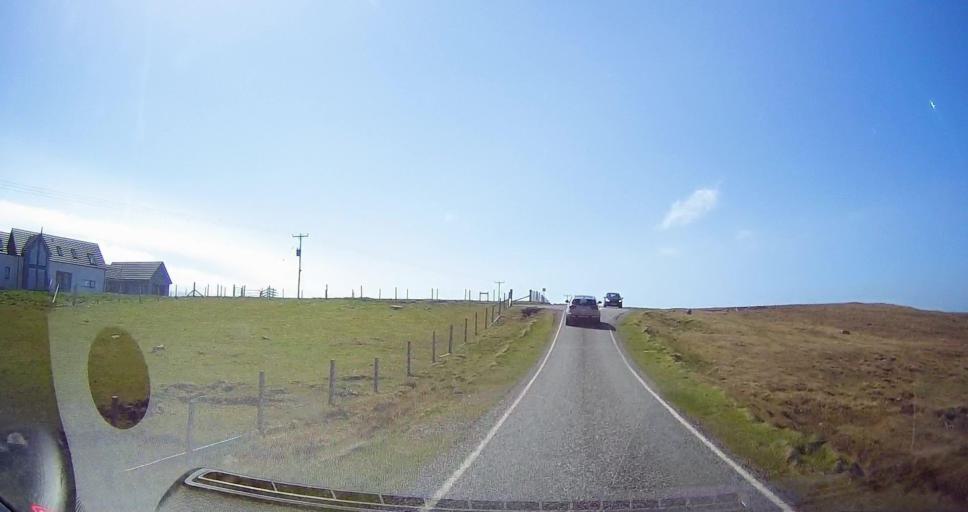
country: GB
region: Scotland
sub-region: Shetland Islands
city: Sandwick
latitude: 60.0931
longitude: -1.3236
